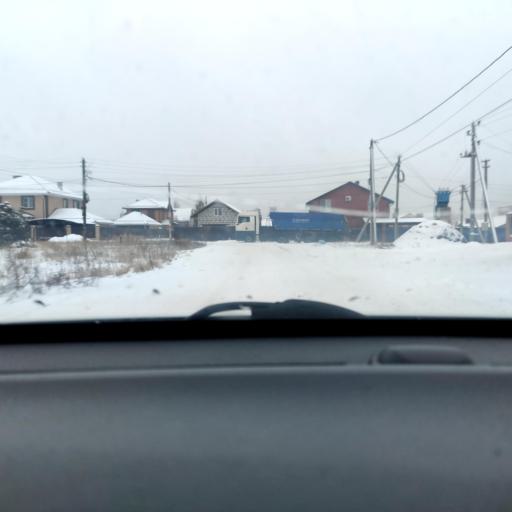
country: RU
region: Voronezj
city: Somovo
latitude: 51.6832
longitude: 39.3180
